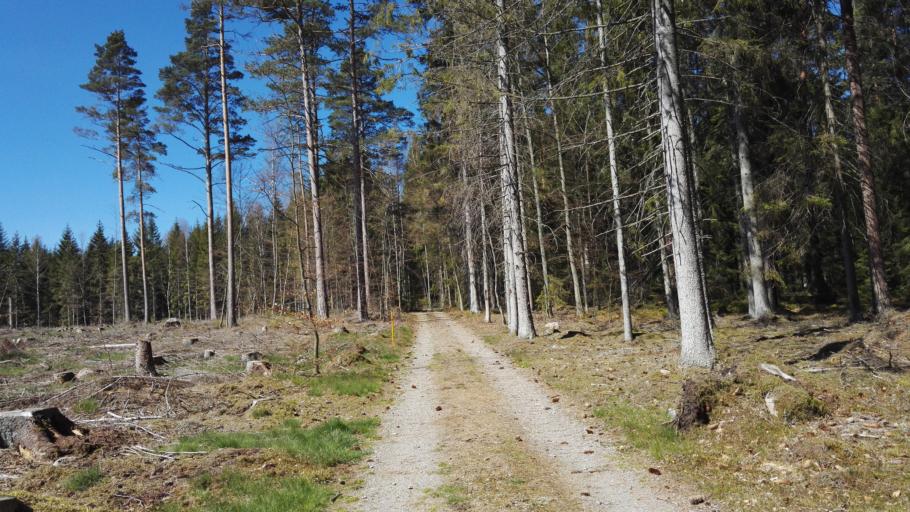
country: SE
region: Kronoberg
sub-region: Vaxjo Kommun
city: Vaexjoe
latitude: 56.9532
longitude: 14.7550
